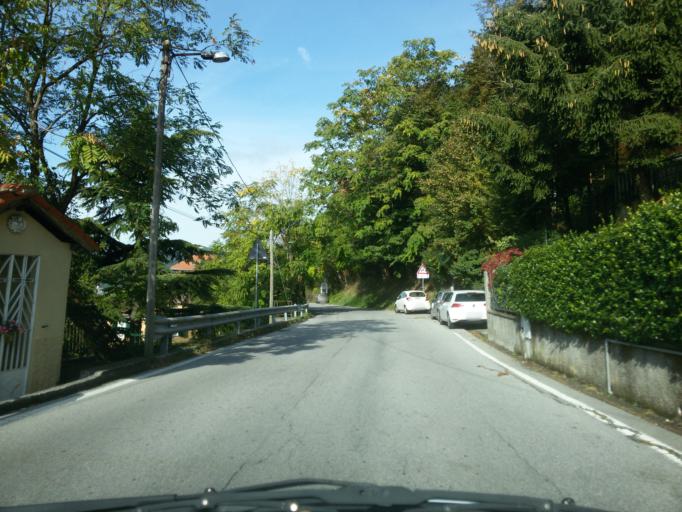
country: IT
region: Liguria
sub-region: Provincia di Genova
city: Piccarello
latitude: 44.4700
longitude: 8.9589
